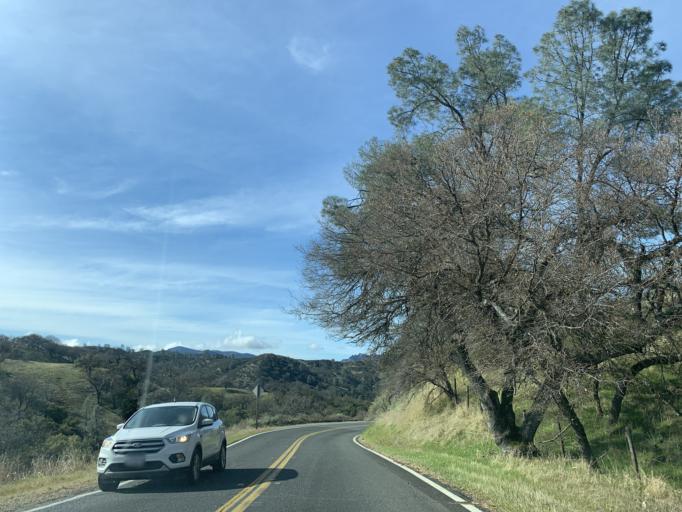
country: US
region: California
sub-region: Monterey County
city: Greenfield
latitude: 36.5074
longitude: -121.1023
